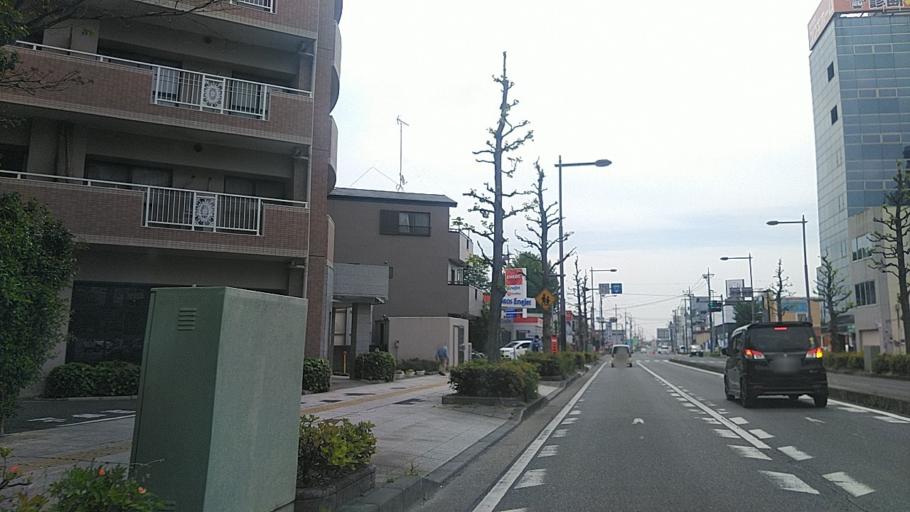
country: JP
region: Saitama
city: Kumagaya
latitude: 36.1406
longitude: 139.3957
